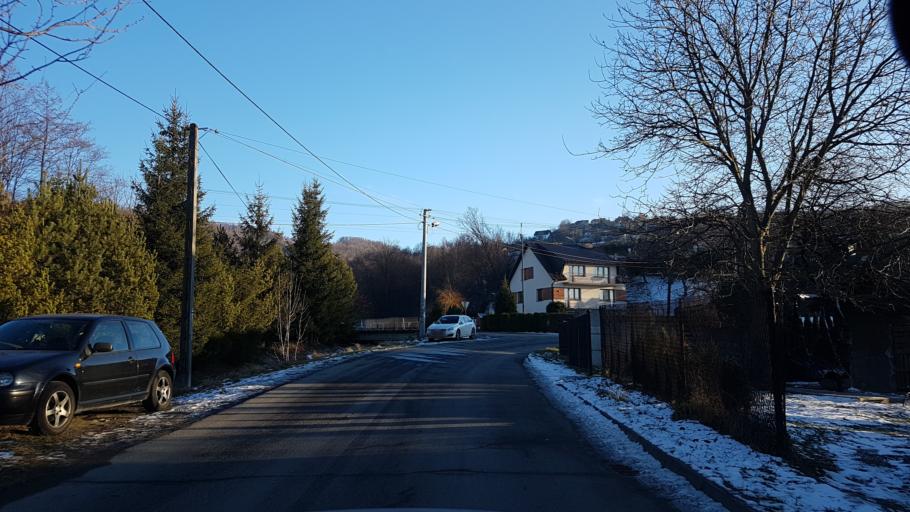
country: PL
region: Lesser Poland Voivodeship
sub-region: Powiat nowosadecki
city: Rytro
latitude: 49.5199
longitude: 20.6631
